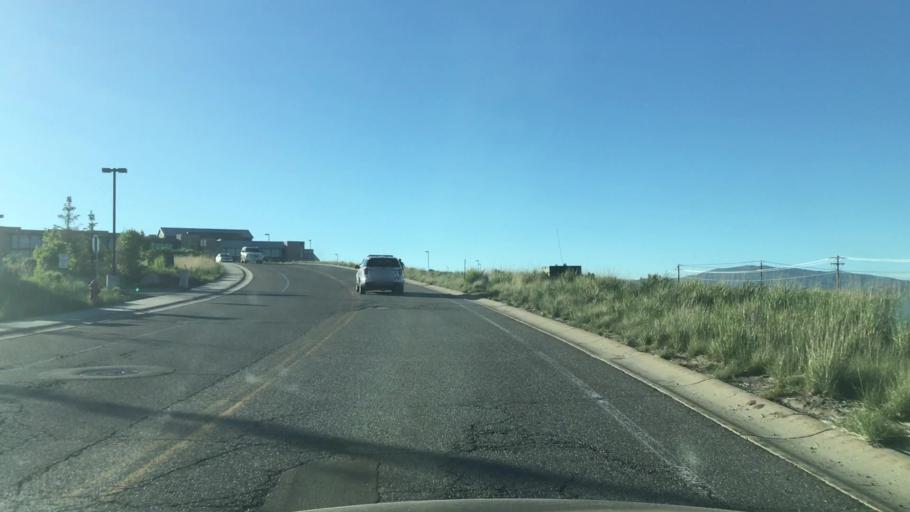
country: US
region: Utah
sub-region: Summit County
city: Park City
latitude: 40.6862
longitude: -111.4663
